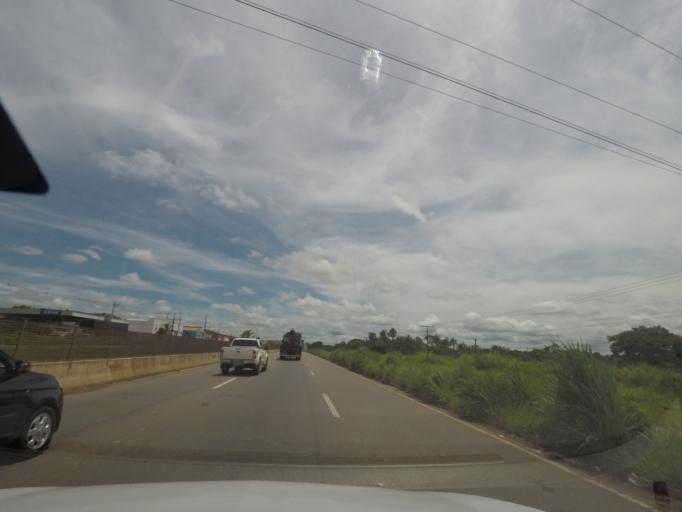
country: BR
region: Goias
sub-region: Goiania
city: Goiania
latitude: -16.7055
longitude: -49.3450
